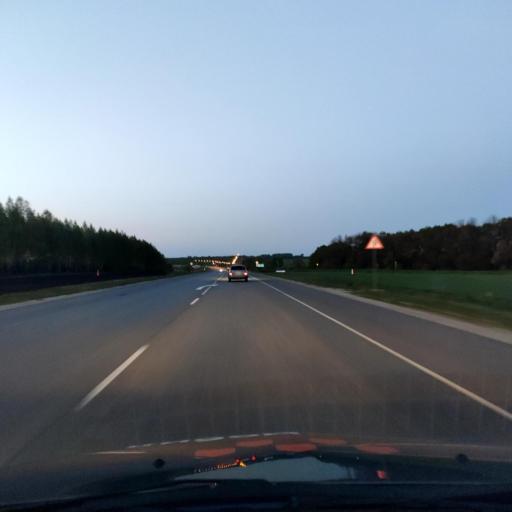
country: RU
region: Orjol
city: Zmiyevka
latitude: 52.7295
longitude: 36.3251
